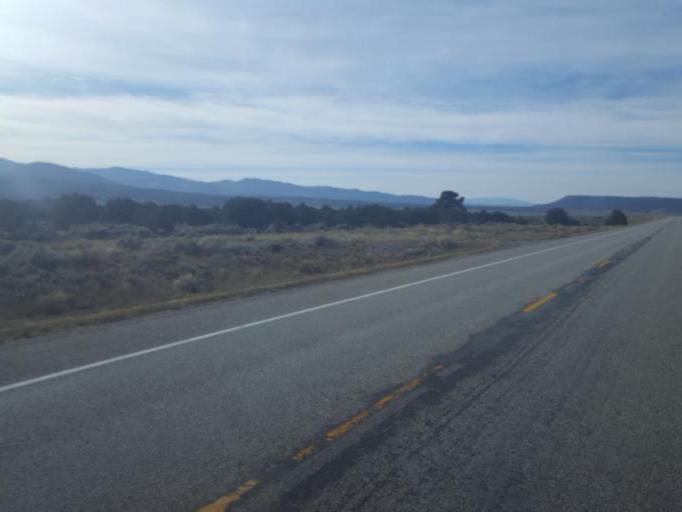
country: US
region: Colorado
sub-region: Costilla County
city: San Luis
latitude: 37.4763
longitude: -105.3482
